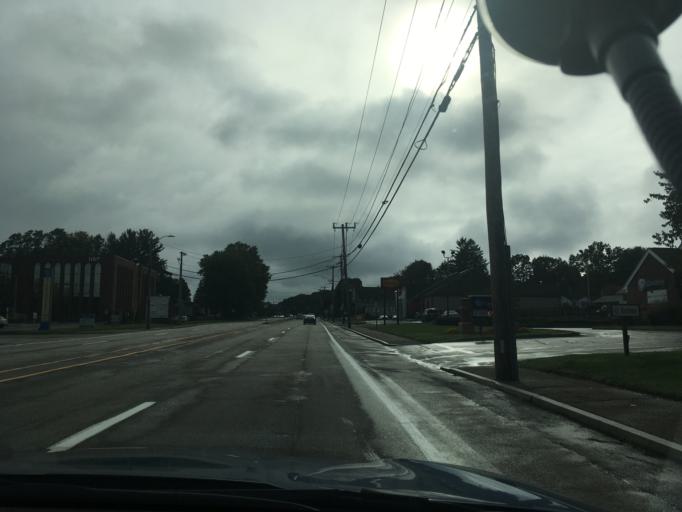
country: US
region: Rhode Island
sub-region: Providence County
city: Cranston
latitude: 41.7701
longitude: -71.4545
